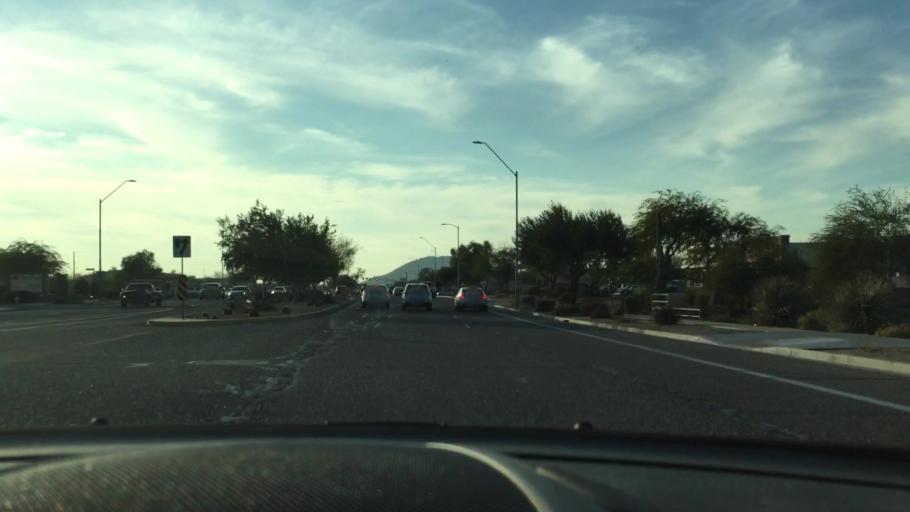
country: US
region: Arizona
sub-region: Maricopa County
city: Sun City
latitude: 33.7123
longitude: -112.1992
